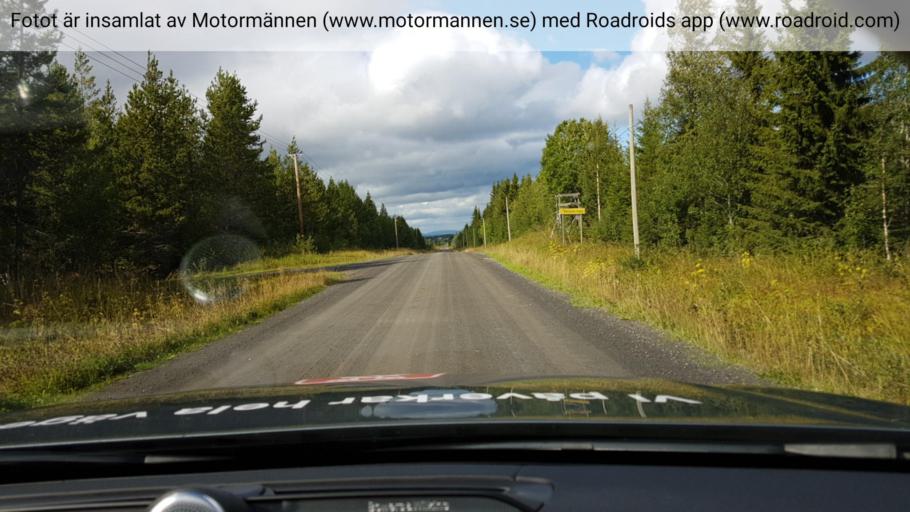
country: SE
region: Jaemtland
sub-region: OEstersunds Kommun
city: Lit
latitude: 63.6215
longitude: 14.9795
